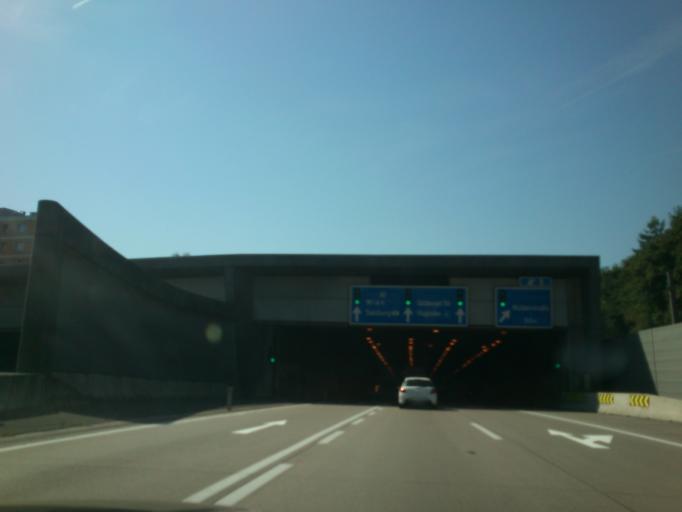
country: AT
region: Upper Austria
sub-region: Linz Stadt
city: Linz
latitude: 48.2766
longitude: 14.2946
